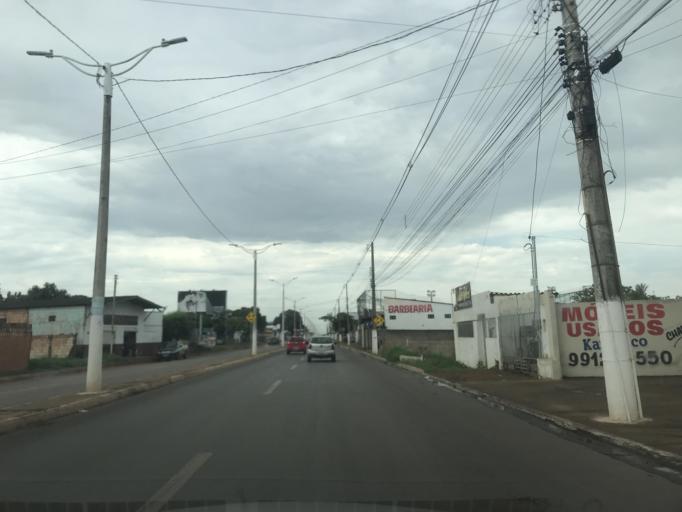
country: BR
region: Goias
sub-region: Luziania
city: Luziania
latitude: -16.2059
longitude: -47.9255
